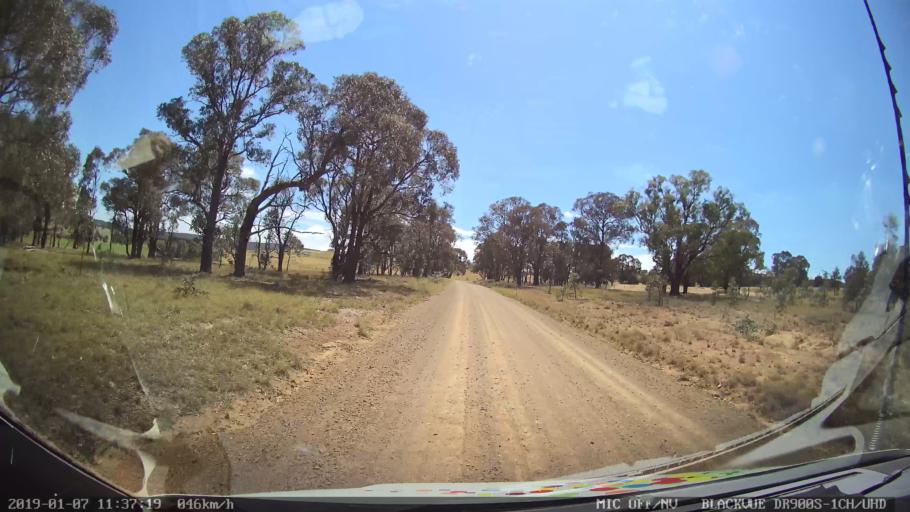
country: AU
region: New South Wales
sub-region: Armidale Dumaresq
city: Armidale
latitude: -30.3714
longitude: 151.5647
